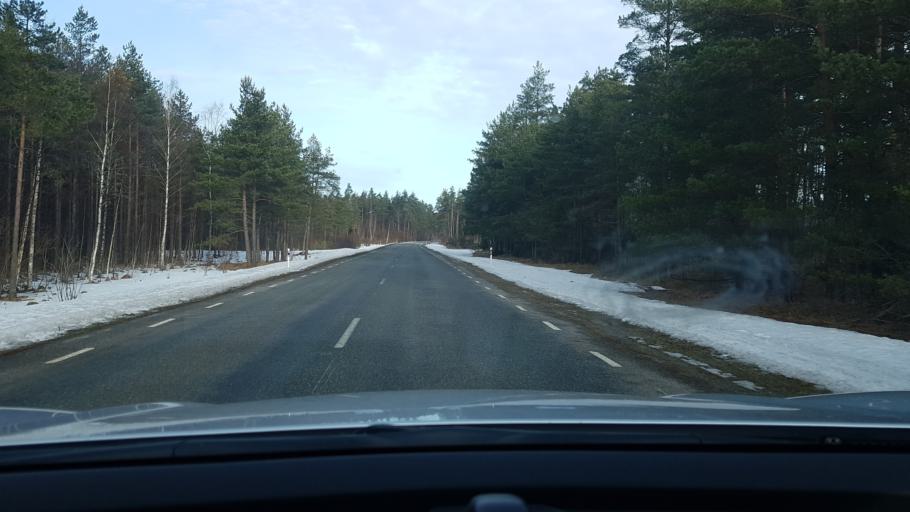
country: EE
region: Saare
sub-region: Kuressaare linn
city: Kuressaare
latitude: 58.4357
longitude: 22.7050
